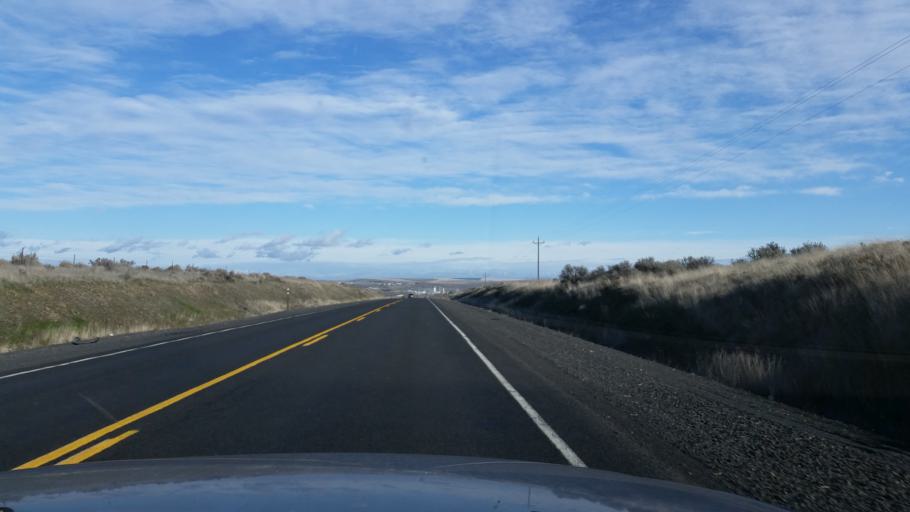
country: US
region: Washington
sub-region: Adams County
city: Ritzville
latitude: 47.3170
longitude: -118.7431
